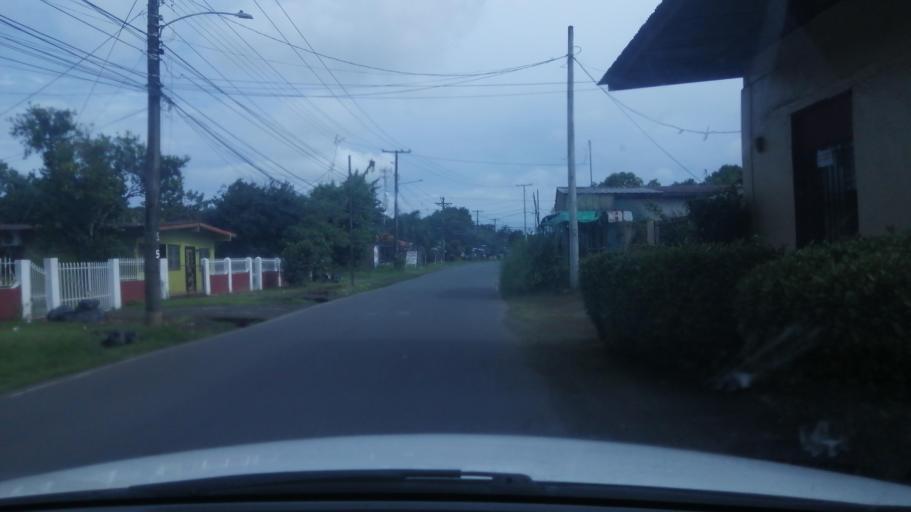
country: PA
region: Chiriqui
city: David
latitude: 8.4228
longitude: -82.4239
